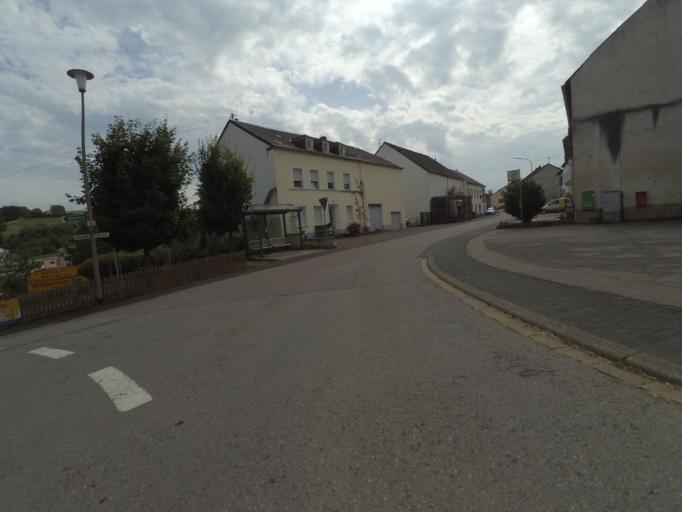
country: DE
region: Rheinland-Pfalz
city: Onsdorf
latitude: 49.6442
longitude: 6.4815
